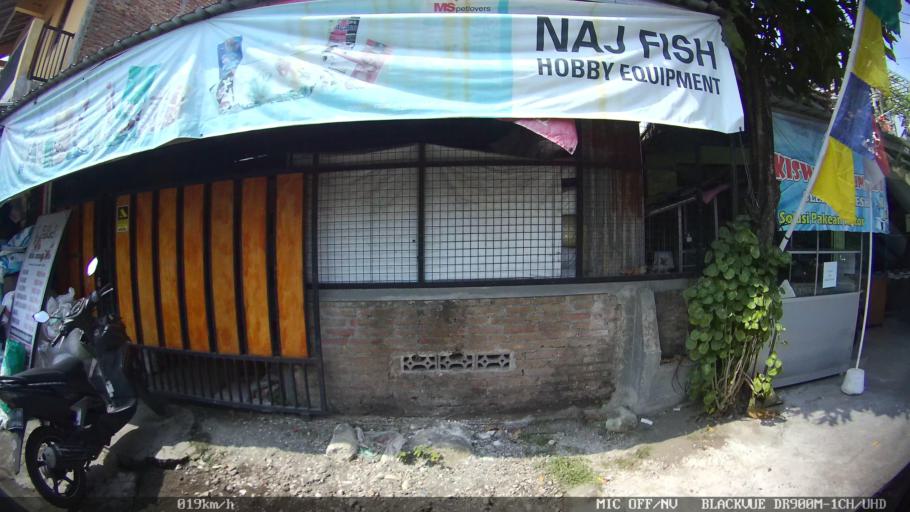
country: ID
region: Daerah Istimewa Yogyakarta
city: Yogyakarta
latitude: -7.8093
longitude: 110.3912
